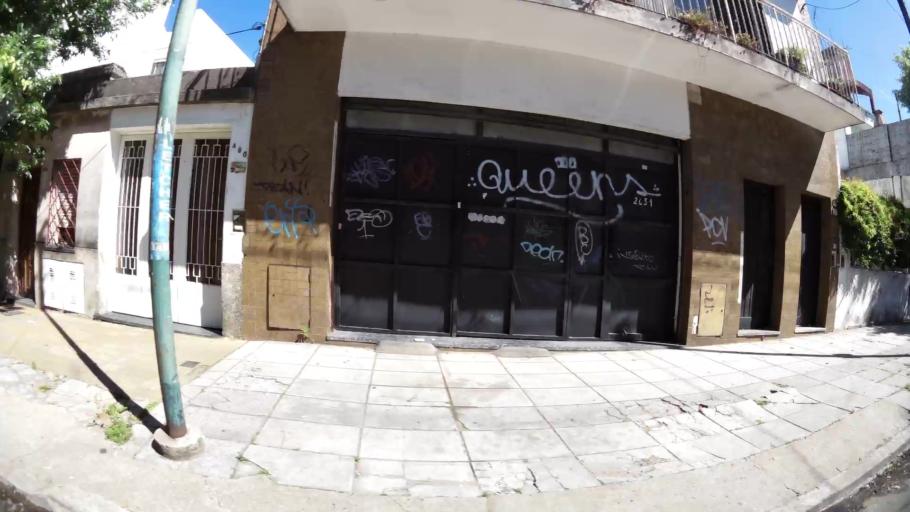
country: AR
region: Buenos Aires
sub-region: Partido de General San Martin
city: General San Martin
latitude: -34.5664
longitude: -58.5334
